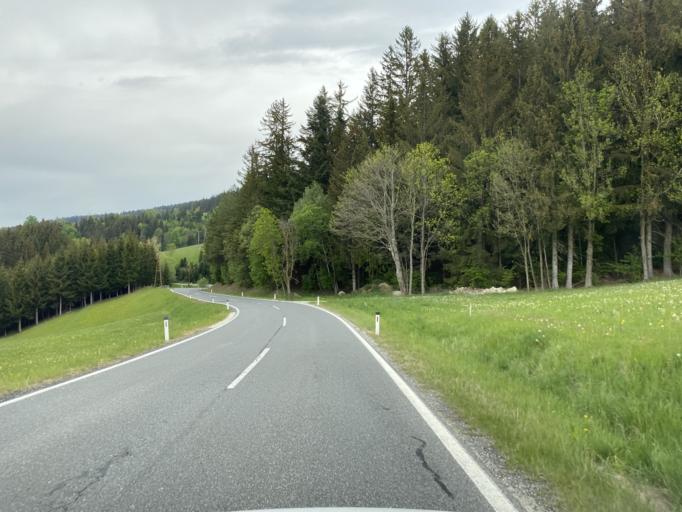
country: AT
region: Styria
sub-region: Politischer Bezirk Weiz
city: Gschaid bei Birkfeld
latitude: 47.3423
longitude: 15.7433
